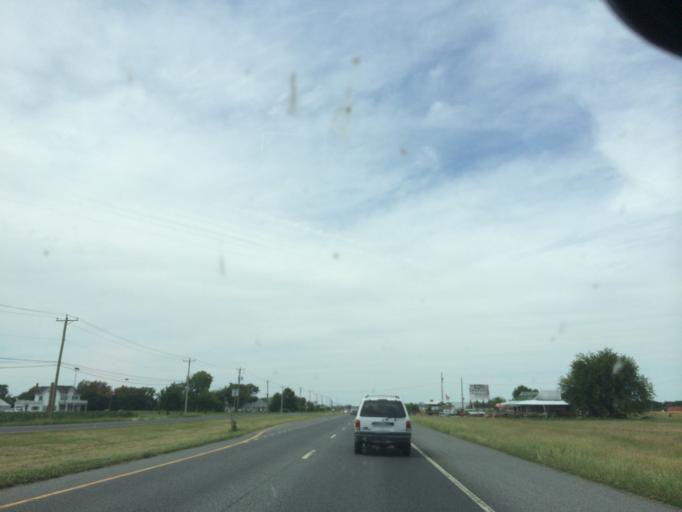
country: US
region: Delaware
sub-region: Sussex County
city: Bridgeville
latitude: 38.7141
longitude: -75.5890
